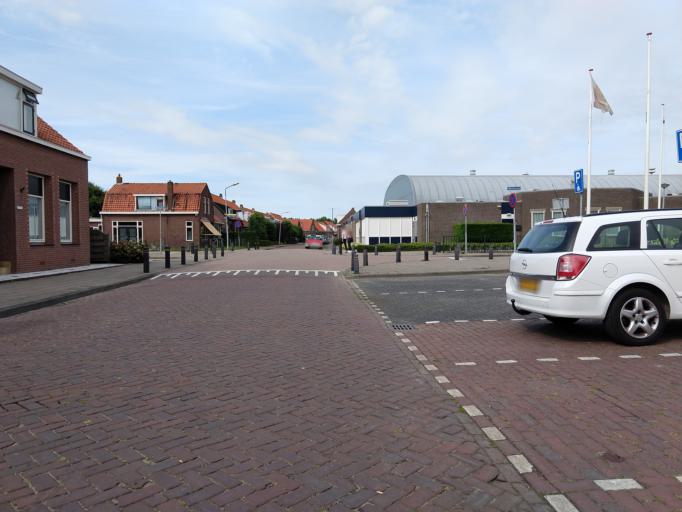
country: NL
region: South Holland
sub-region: Gemeente Goeree-Overflakkee
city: Middelharnis
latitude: 51.6930
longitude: 4.2133
